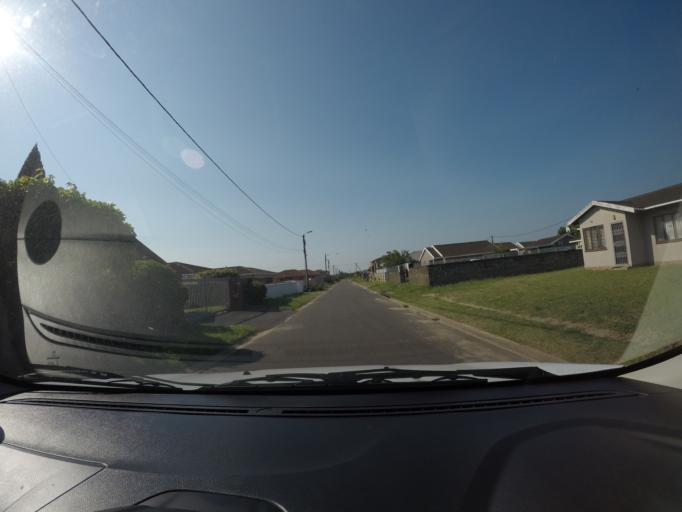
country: ZA
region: KwaZulu-Natal
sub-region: uThungulu District Municipality
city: Richards Bay
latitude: -28.7240
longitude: 32.0359
